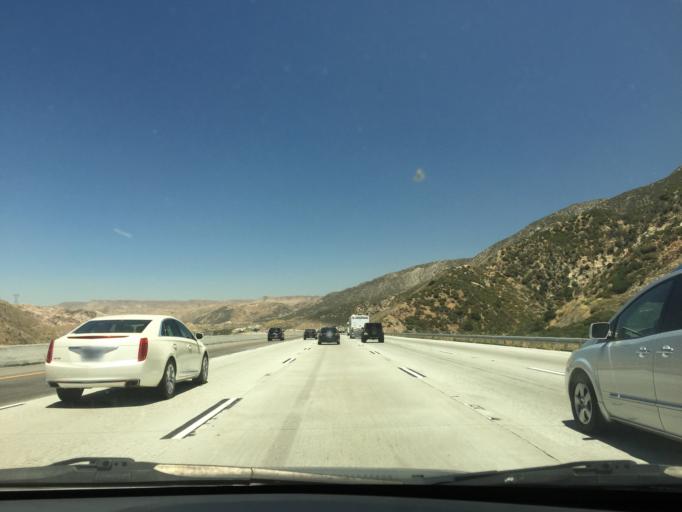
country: US
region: California
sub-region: San Bernardino County
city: Oak Hills
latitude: 34.2649
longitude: -117.4494
